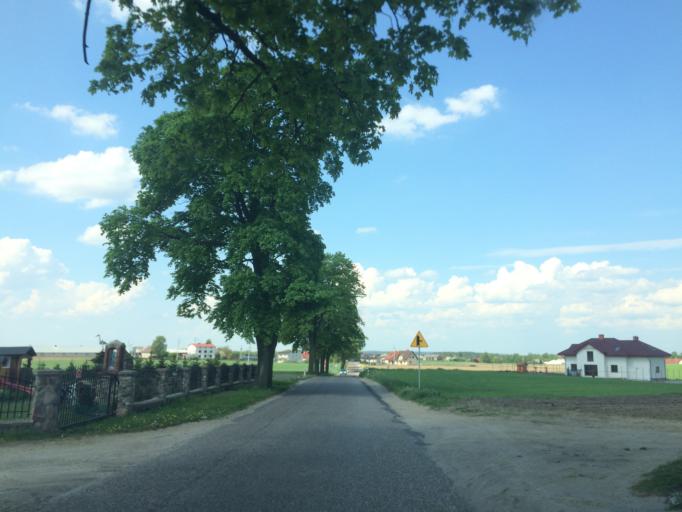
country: PL
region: Warmian-Masurian Voivodeship
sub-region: Powiat ilawski
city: Lubawa
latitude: 53.4099
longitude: 19.7790
